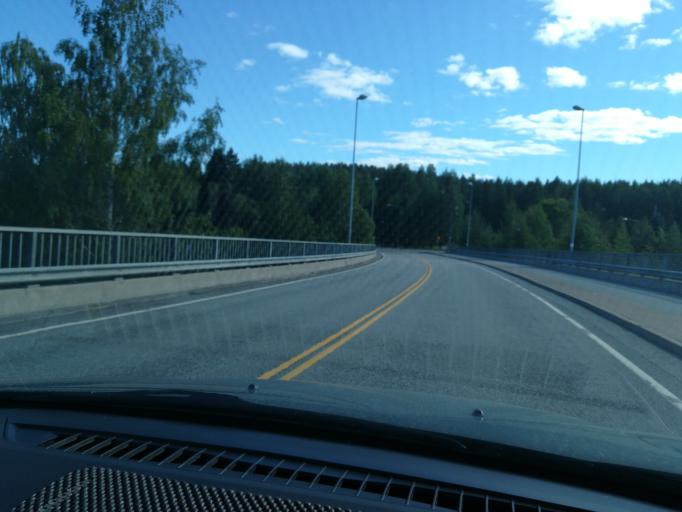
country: FI
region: Southern Savonia
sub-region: Mikkeli
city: Puumala
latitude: 61.5172
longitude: 28.1734
